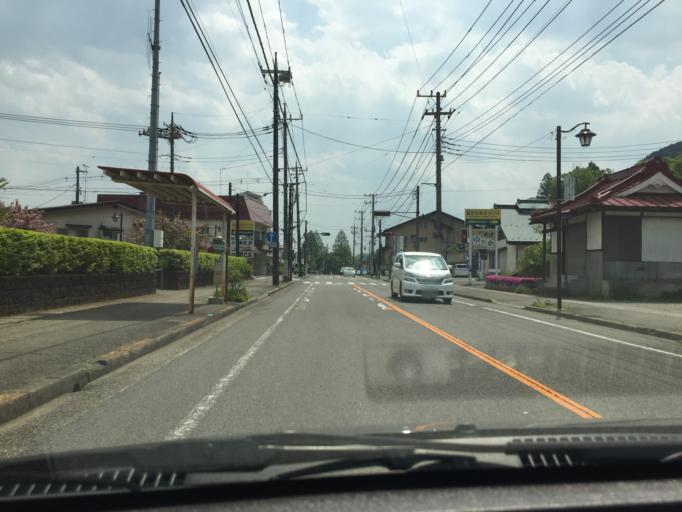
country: JP
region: Tochigi
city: Imaichi
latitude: 36.8315
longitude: 139.7161
